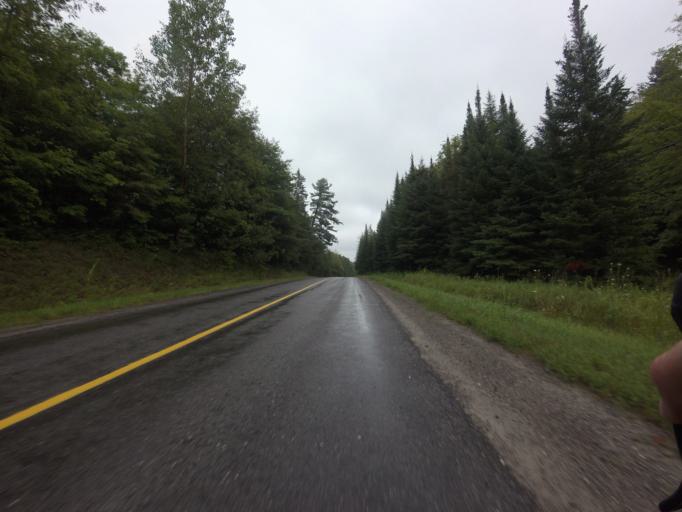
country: CA
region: Ontario
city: Perth
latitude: 45.0603
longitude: -76.5659
